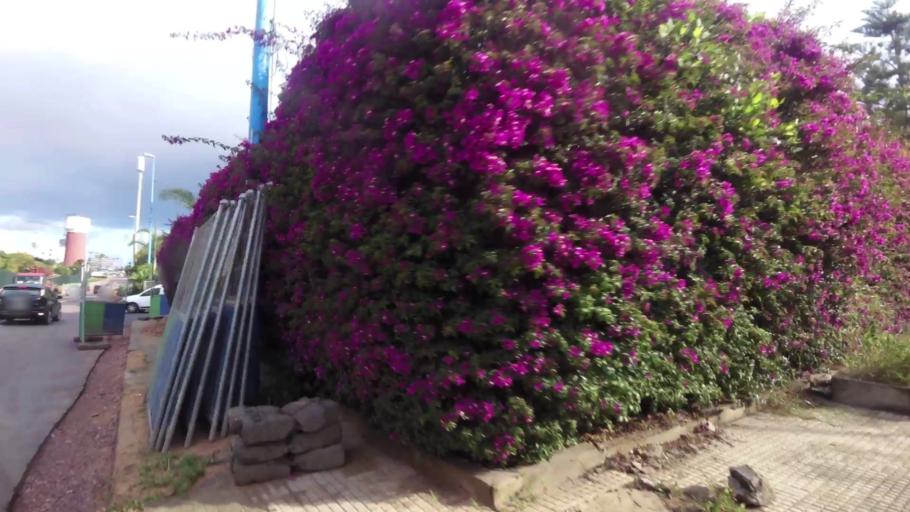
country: MA
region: Grand Casablanca
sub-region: Casablanca
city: Casablanca
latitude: 33.5537
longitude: -7.6483
